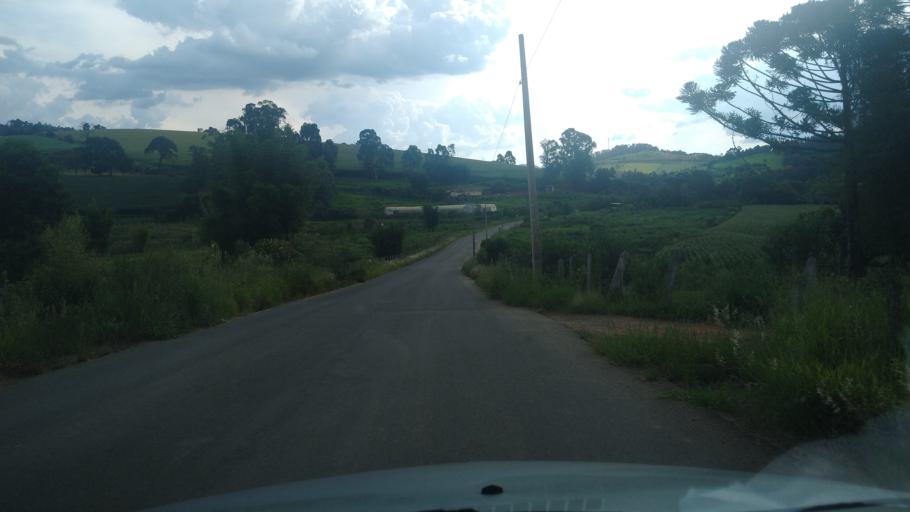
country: BR
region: Minas Gerais
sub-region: Extrema
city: Extrema
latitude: -22.7263
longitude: -46.3526
